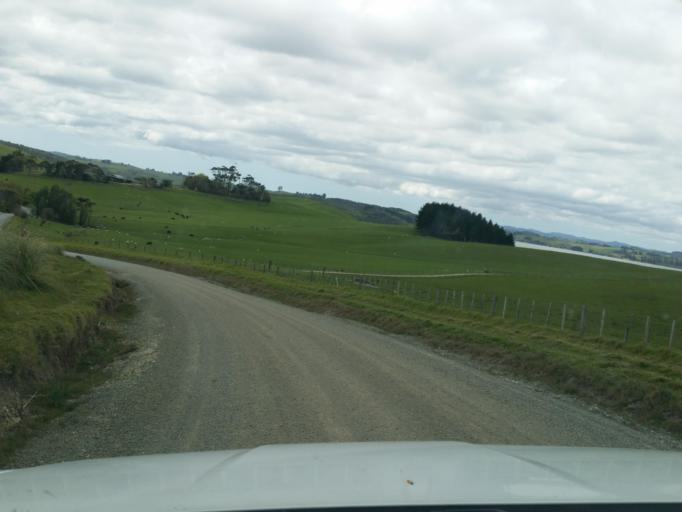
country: NZ
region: Auckland
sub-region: Auckland
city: Wellsford
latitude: -36.2869
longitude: 174.3516
